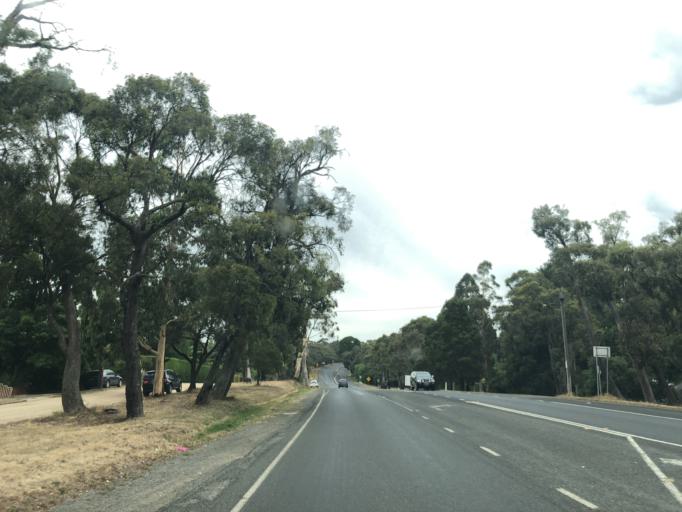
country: AU
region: Victoria
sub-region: Hume
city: Sunbury
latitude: -37.3619
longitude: 144.5274
